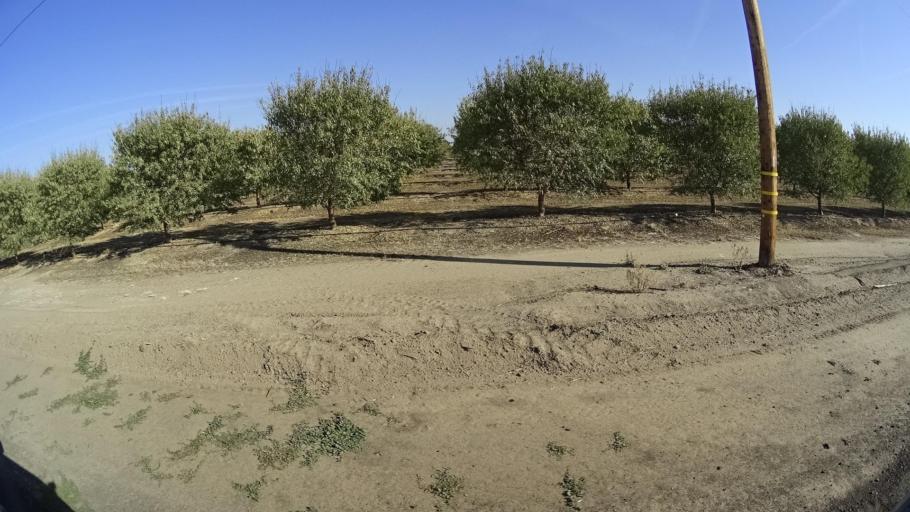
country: US
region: California
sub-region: Kern County
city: Wasco
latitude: 35.6686
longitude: -119.3840
